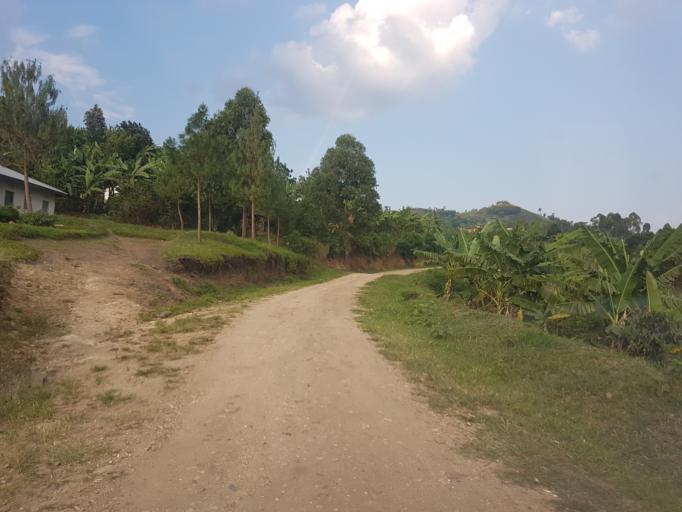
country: UG
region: Western Region
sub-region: Rukungiri District
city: Rukungiri
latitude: -0.6760
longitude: 29.8975
